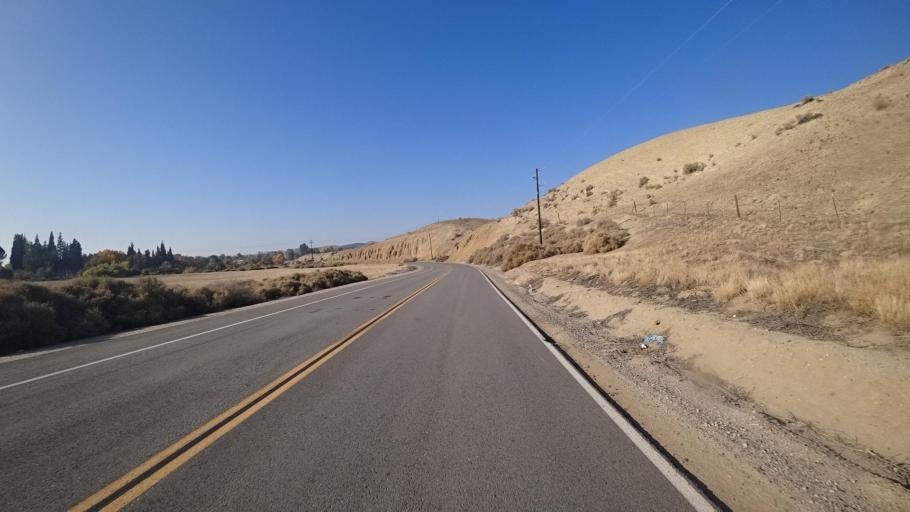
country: US
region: California
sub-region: Kern County
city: Oildale
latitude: 35.4499
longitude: -118.9021
